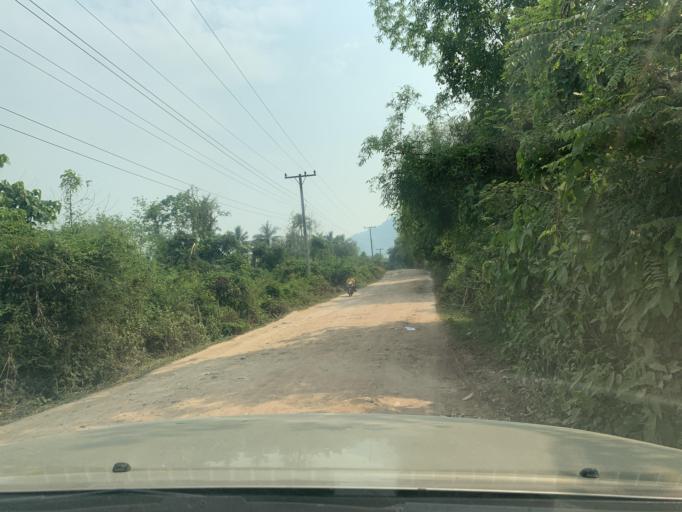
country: LA
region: Louangphabang
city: Louangphabang
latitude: 19.9097
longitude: 102.1341
